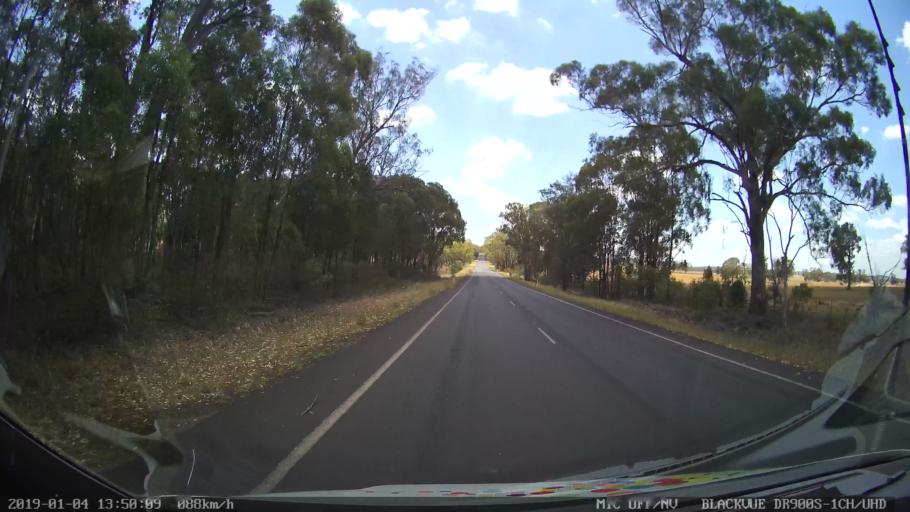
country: AU
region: New South Wales
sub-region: Dubbo Municipality
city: Dubbo
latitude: -32.4234
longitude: 148.5747
